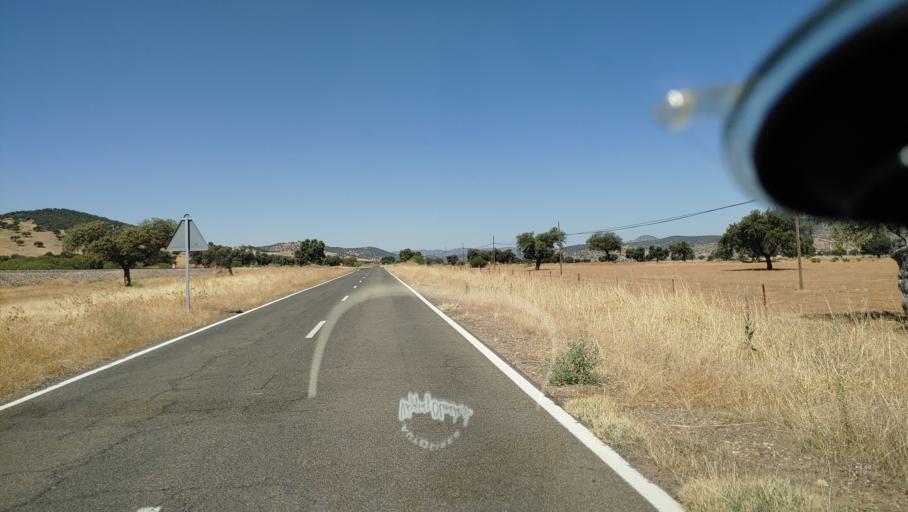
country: ES
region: Castille-La Mancha
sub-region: Provincia de Ciudad Real
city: Guadalmez
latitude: 38.7061
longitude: -4.9505
